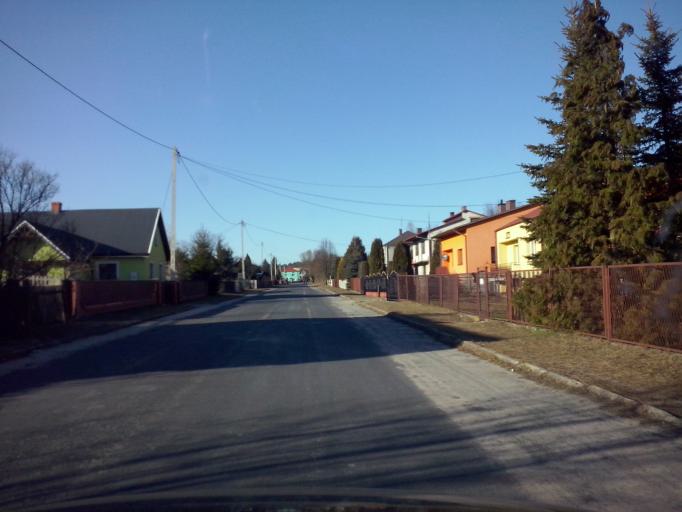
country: PL
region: Subcarpathian Voivodeship
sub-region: Powiat nizanski
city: Harasiuki
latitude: 50.5251
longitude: 22.4515
